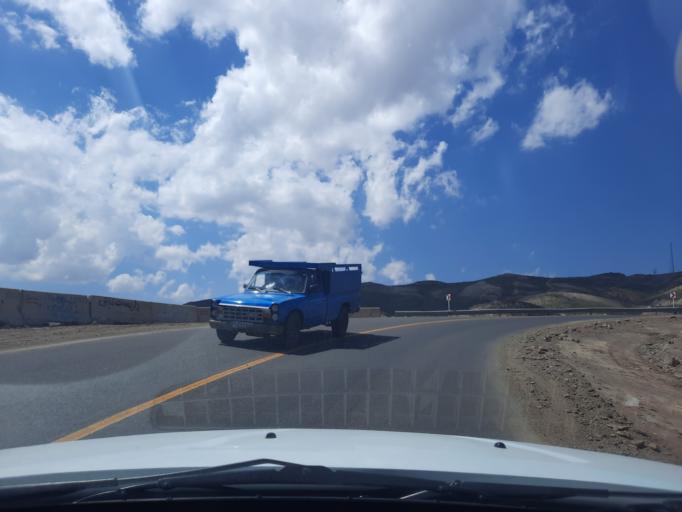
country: IR
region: Qazvin
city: Qazvin
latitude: 36.3773
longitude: 50.2105
